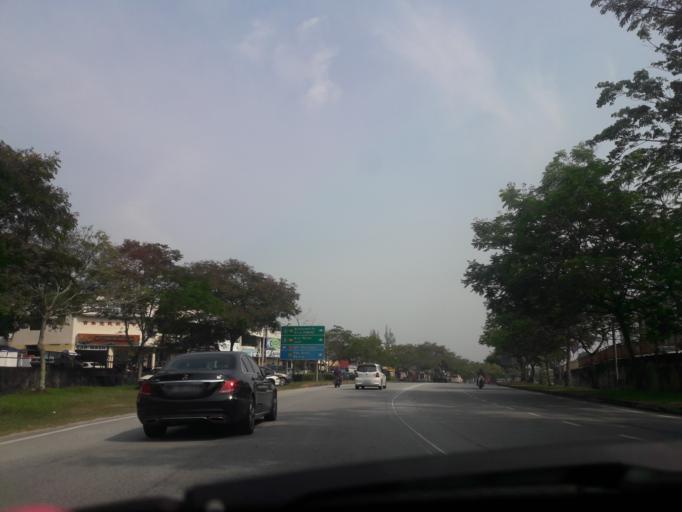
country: MY
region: Kedah
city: Kulim
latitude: 5.3696
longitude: 100.5424
